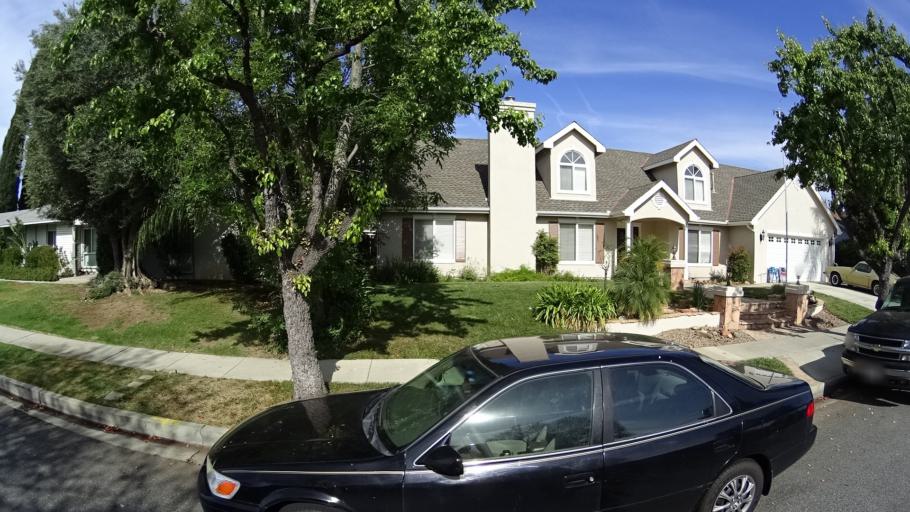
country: US
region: California
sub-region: Ventura County
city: Thousand Oaks
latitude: 34.1973
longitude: -118.8750
